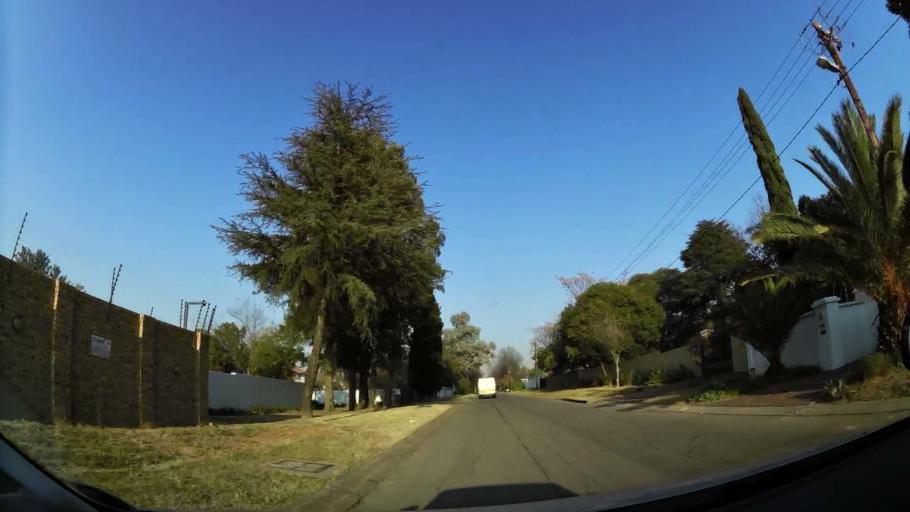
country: ZA
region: Gauteng
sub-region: City of Johannesburg Metropolitan Municipality
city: Modderfontein
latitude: -26.0829
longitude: 28.1004
